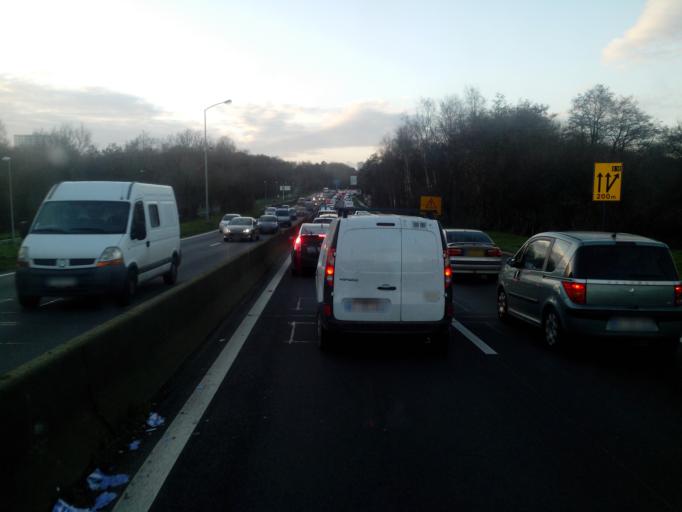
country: FR
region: Pays de la Loire
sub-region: Departement de la Loire-Atlantique
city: La Chapelle-sur-Erdre
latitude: 47.2572
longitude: -1.5483
